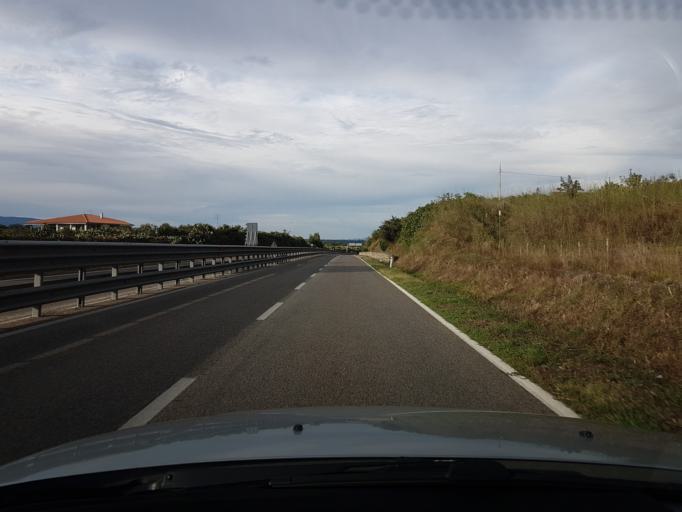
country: IT
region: Sardinia
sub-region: Provincia di Oristano
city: Ghilarza
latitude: 40.1240
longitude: 8.8510
